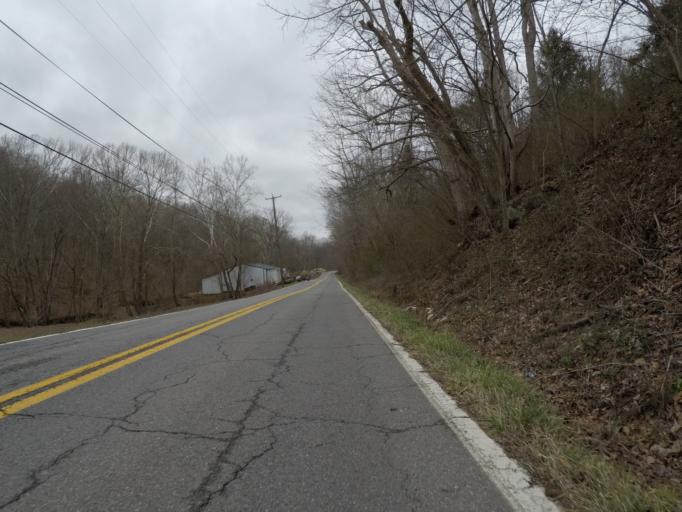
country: US
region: West Virginia
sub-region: Cabell County
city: Lesage
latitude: 38.4696
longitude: -82.2889
